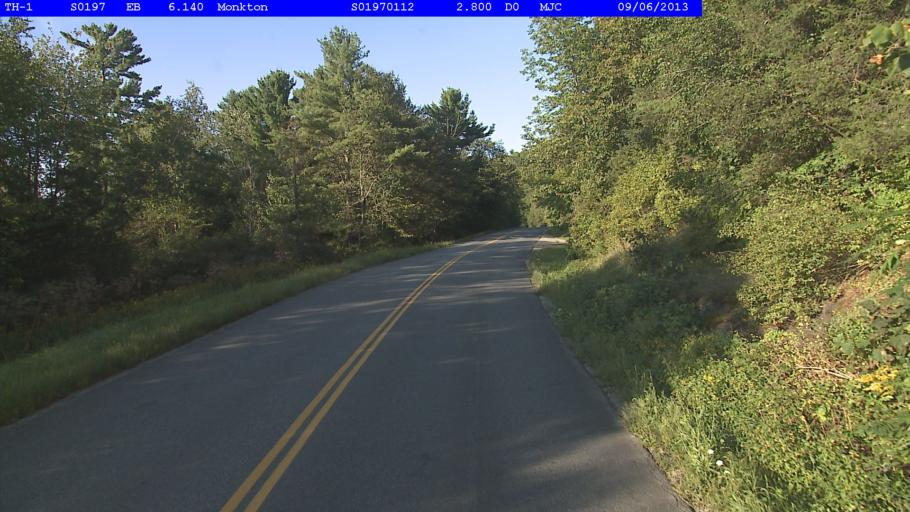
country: US
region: Vermont
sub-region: Addison County
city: Vergennes
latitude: 44.2183
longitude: -73.1547
